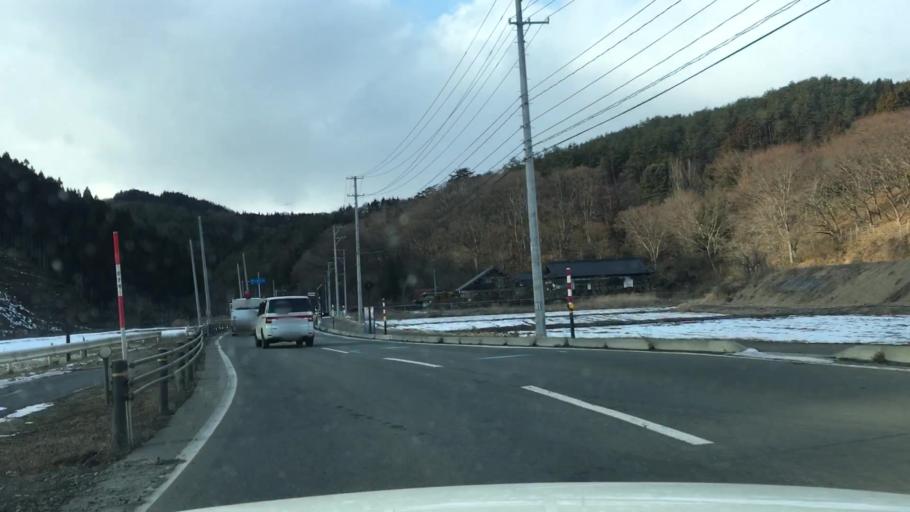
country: JP
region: Iwate
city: Morioka-shi
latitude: 39.6742
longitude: 141.2294
